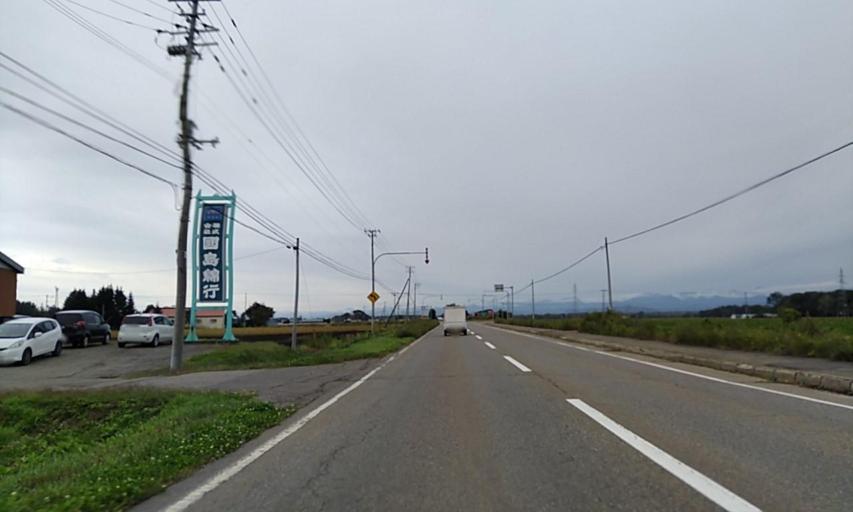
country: JP
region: Hokkaido
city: Obihiro
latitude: 42.7881
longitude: 143.1603
